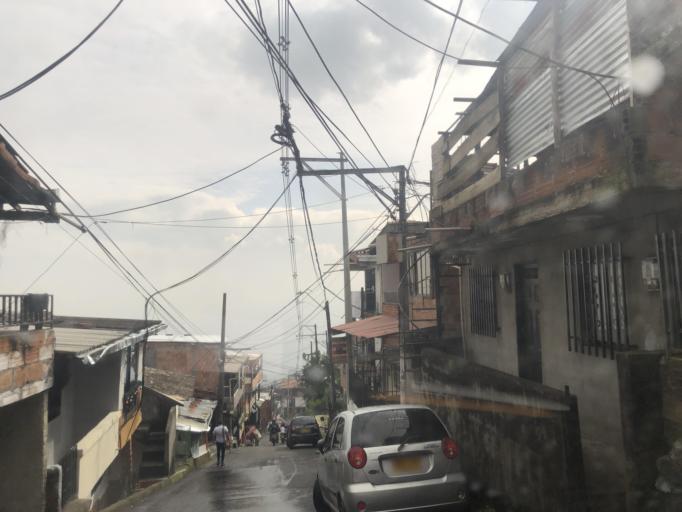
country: CO
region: Antioquia
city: Bello
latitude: 6.3155
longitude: -75.5845
